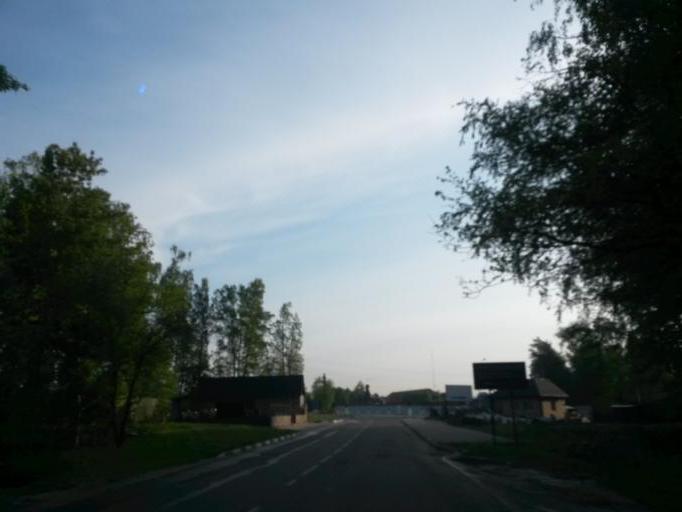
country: RU
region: Moskovskaya
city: Shcherbinka
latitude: 55.5039
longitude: 37.6171
